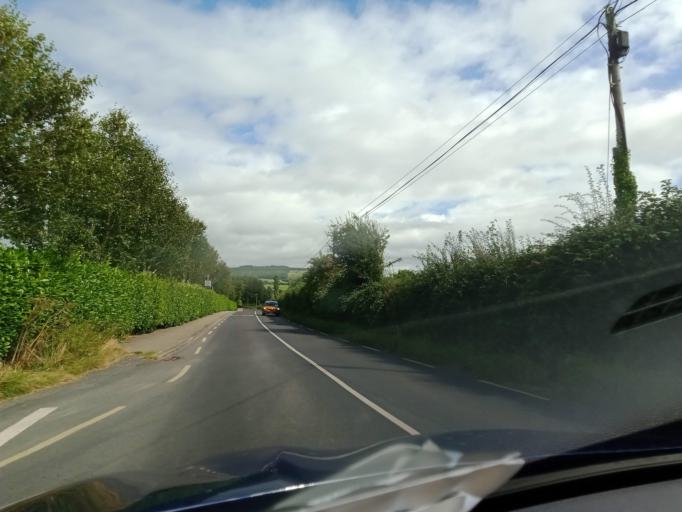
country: IE
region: Leinster
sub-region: Laois
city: Abbeyleix
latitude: 52.9466
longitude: -7.3098
